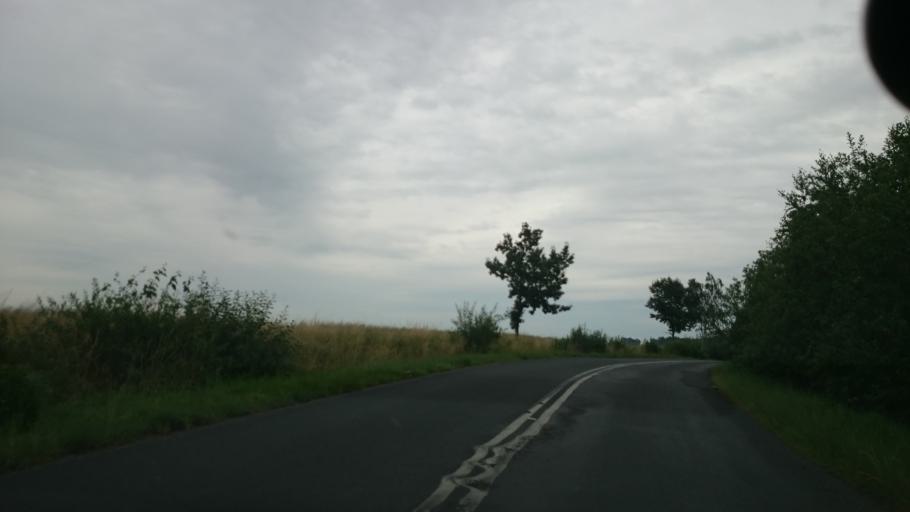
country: PL
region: Lower Silesian Voivodeship
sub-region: Powiat strzelinski
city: Przeworno
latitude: 50.6571
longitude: 17.2417
